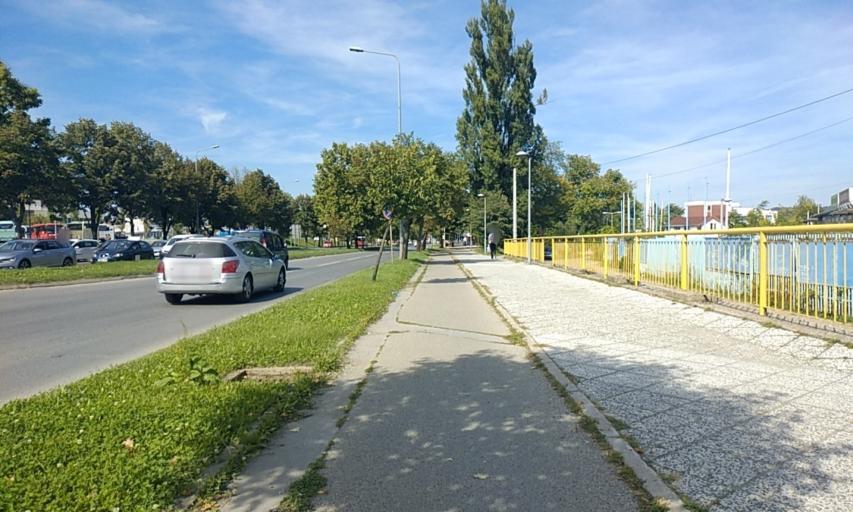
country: BA
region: Republika Srpska
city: Banja Luka
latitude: 44.7838
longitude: 17.2060
